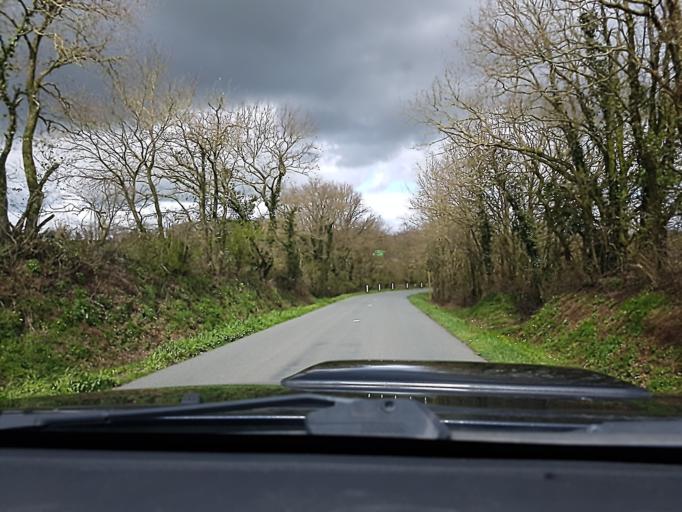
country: FR
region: Pays de la Loire
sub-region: Departement de la Vendee
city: Mache
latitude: 46.7757
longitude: -1.6670
